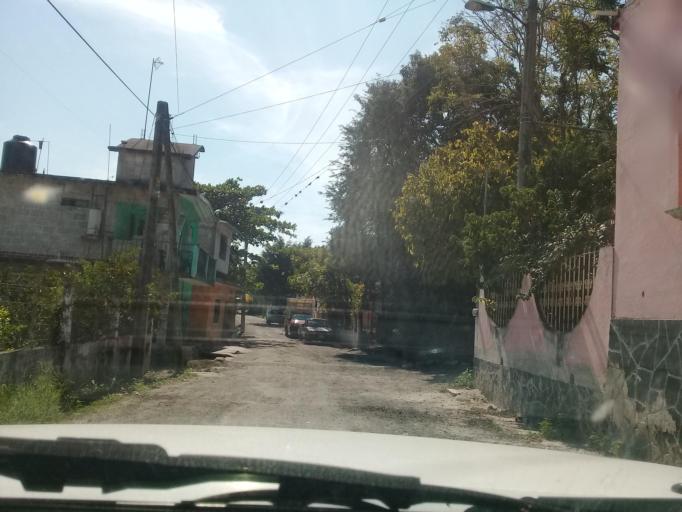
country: MX
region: Veracruz
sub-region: Emiliano Zapata
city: Plan del Rio
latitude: 19.4282
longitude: -96.6129
